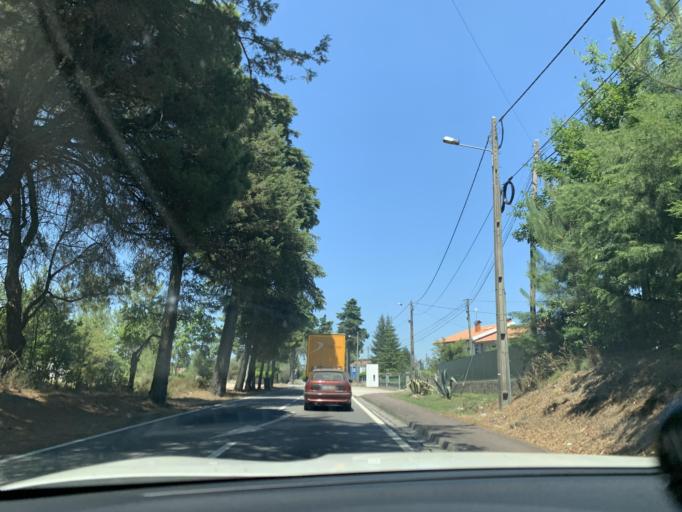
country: PT
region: Viseu
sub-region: Mangualde
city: Mangualde
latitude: 40.5795
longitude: -7.8076
